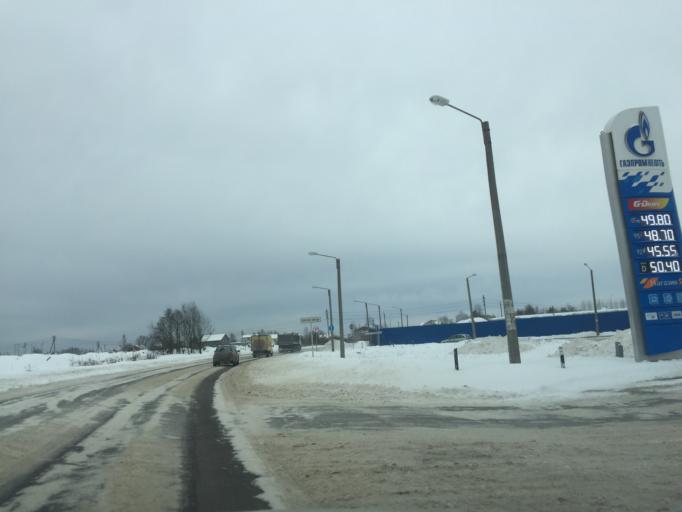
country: RU
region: Leningrad
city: Imeni Sverdlova
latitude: 59.7989
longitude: 30.6672
